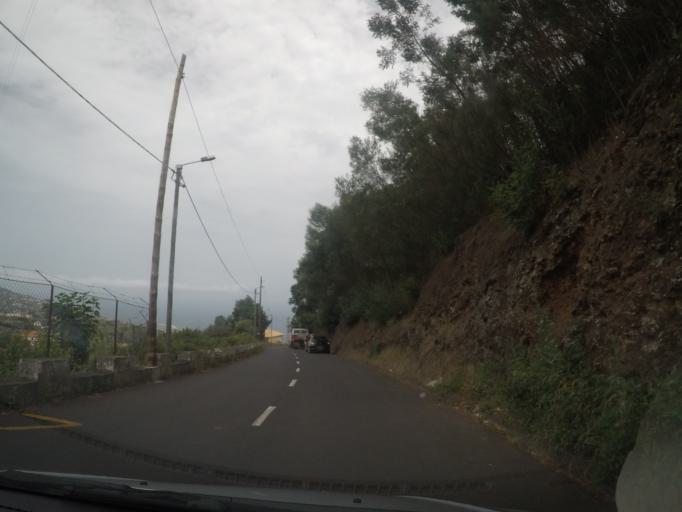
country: PT
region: Madeira
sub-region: Santa Cruz
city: Santa Cruz
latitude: 32.6867
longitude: -16.8135
